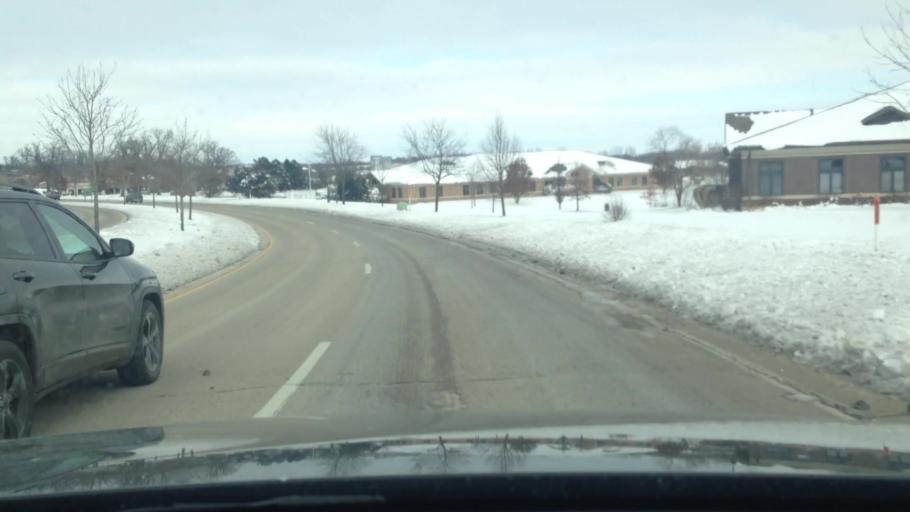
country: US
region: Wisconsin
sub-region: Walworth County
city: Lake Geneva
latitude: 42.5861
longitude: -88.4117
